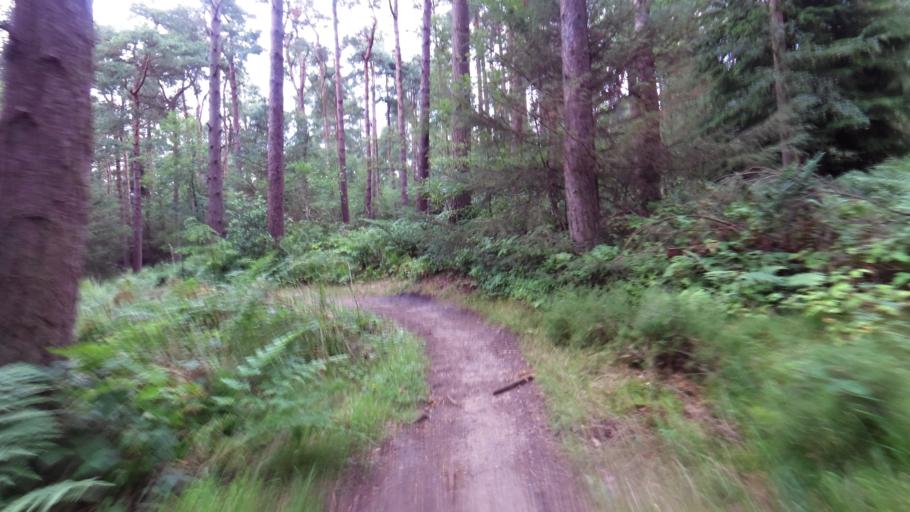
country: GB
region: England
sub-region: North Yorkshire
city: Thornton Dale
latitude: 54.2924
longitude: -0.6707
